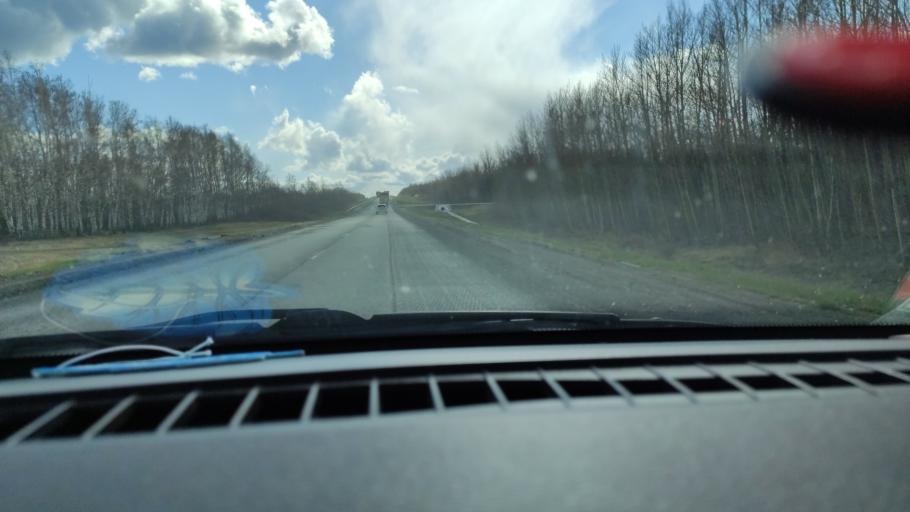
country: RU
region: Saratov
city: Dukhovnitskoye
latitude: 52.6891
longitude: 48.2417
